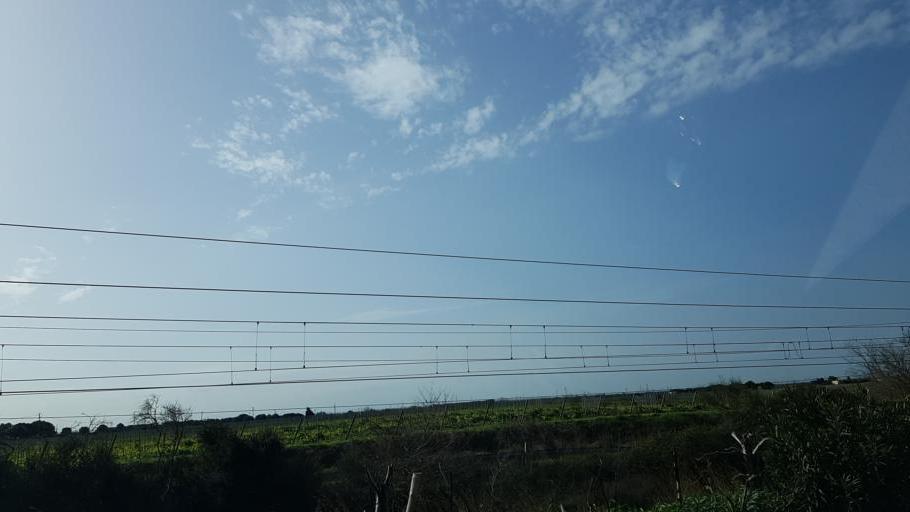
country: IT
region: Apulia
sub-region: Provincia di Brindisi
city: Brindisi
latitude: 40.6243
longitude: 17.8957
